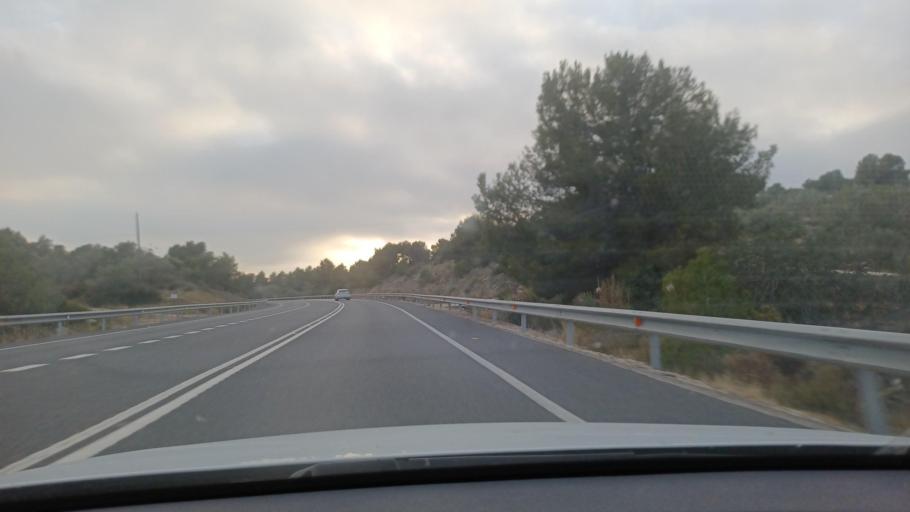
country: ES
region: Catalonia
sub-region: Provincia de Tarragona
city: El Perello
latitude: 40.8605
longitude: 0.7182
